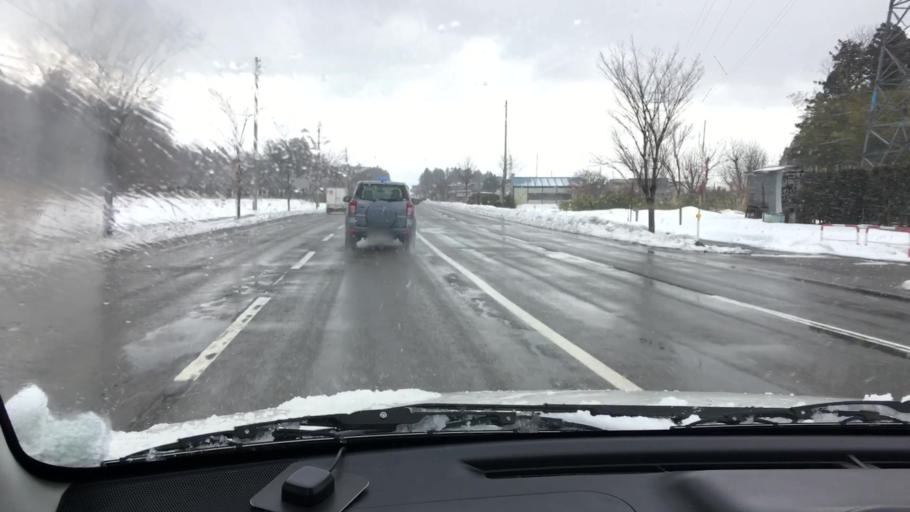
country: JP
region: Niigata
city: Joetsu
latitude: 37.0993
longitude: 138.2309
